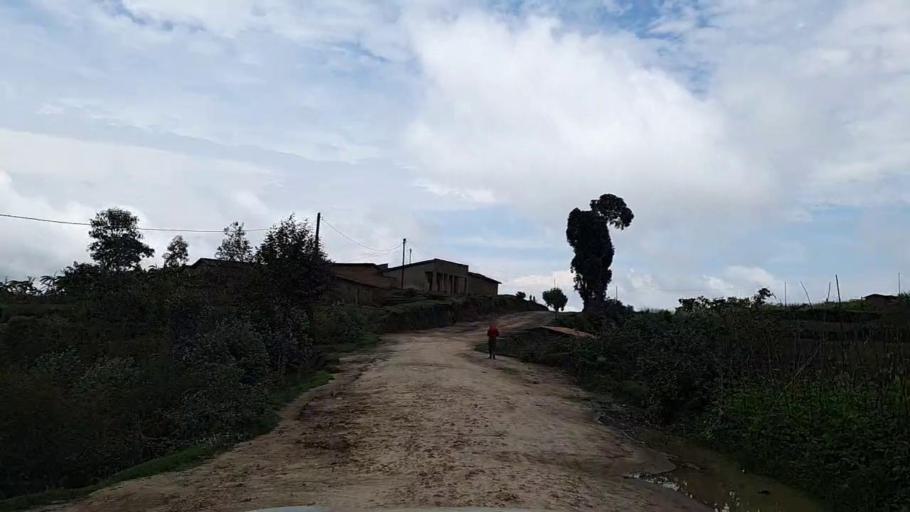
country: RW
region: Southern Province
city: Gikongoro
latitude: -2.3456
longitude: 29.5067
